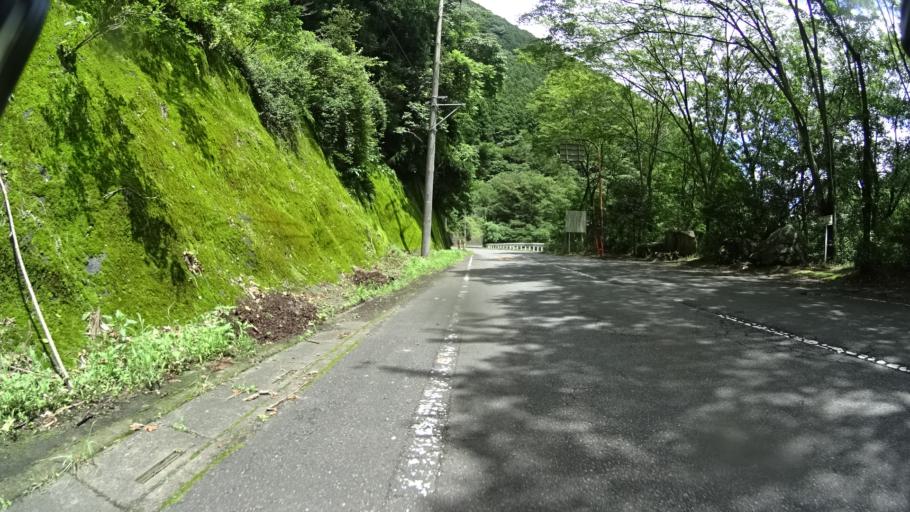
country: JP
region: Tokyo
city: Ome
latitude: 35.8750
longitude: 139.1593
